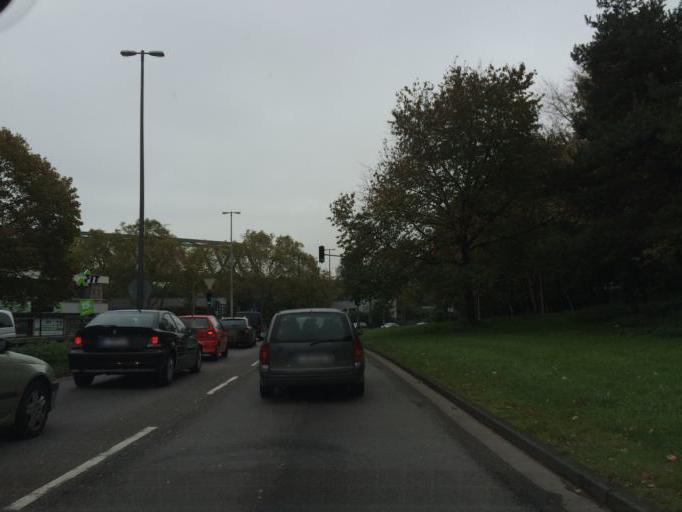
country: DE
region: North Rhine-Westphalia
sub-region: Regierungsbezirk Koln
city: Neuehrenfeld
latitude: 50.9525
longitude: 6.9384
